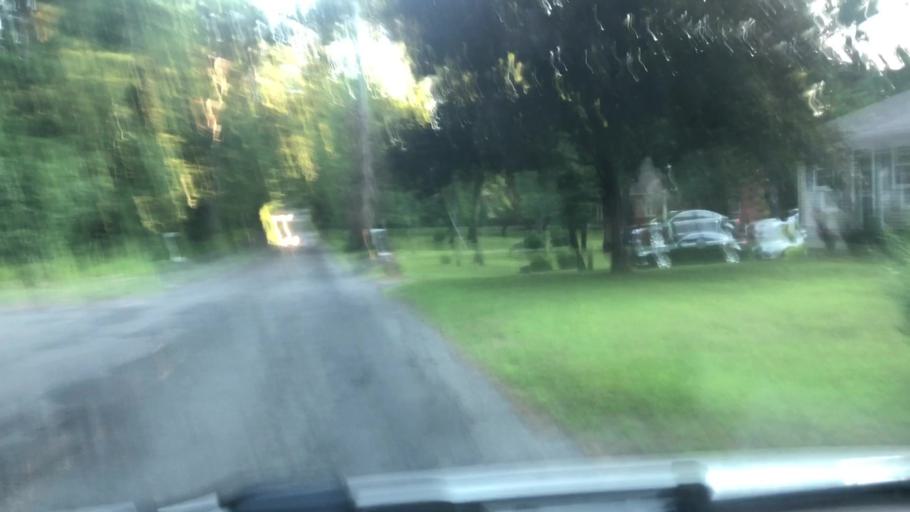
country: US
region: Massachusetts
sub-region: Hampshire County
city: Easthampton
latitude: 42.2848
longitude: -72.7140
